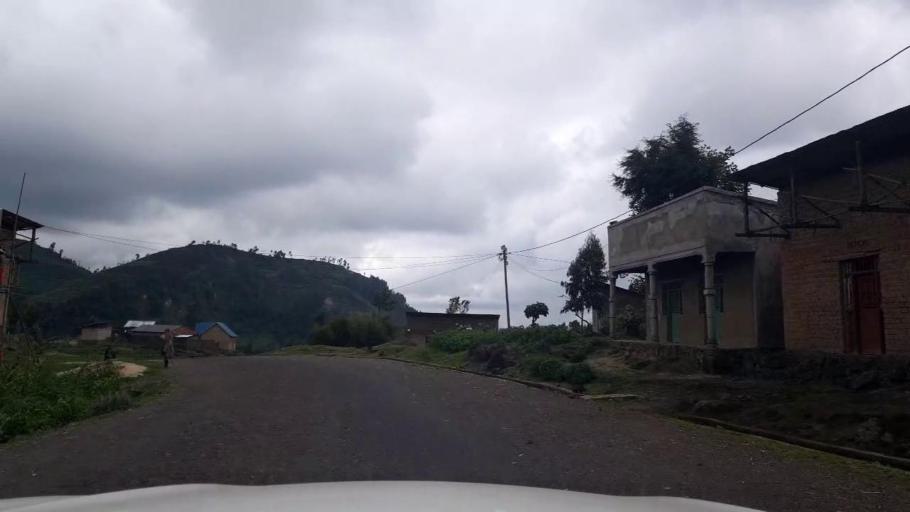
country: RW
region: Northern Province
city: Musanze
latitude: -1.5848
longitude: 29.4729
